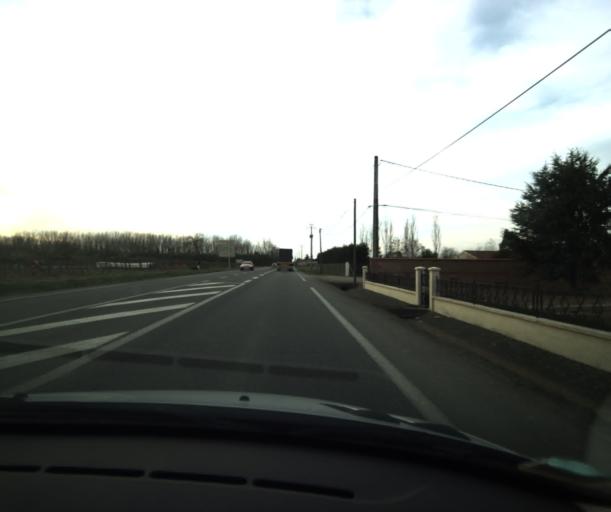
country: FR
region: Midi-Pyrenees
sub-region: Departement du Tarn-et-Garonne
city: Castelsarrasin
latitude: 44.0290
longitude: 1.1356
